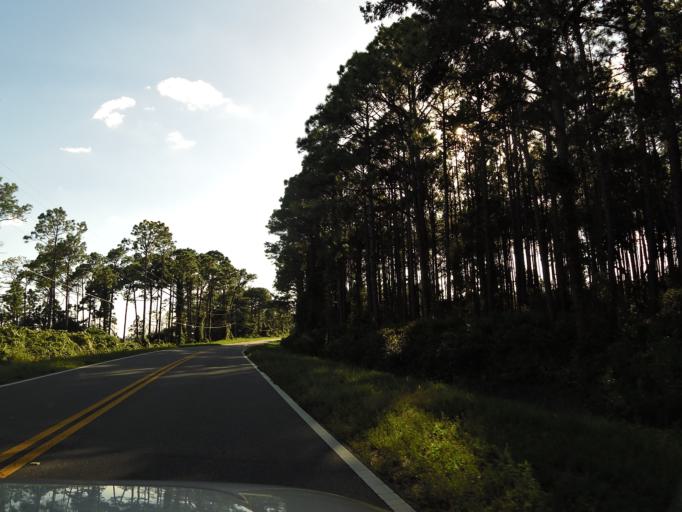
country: US
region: Florida
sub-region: Franklin County
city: Carrabelle
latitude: 29.9125
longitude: -84.5320
